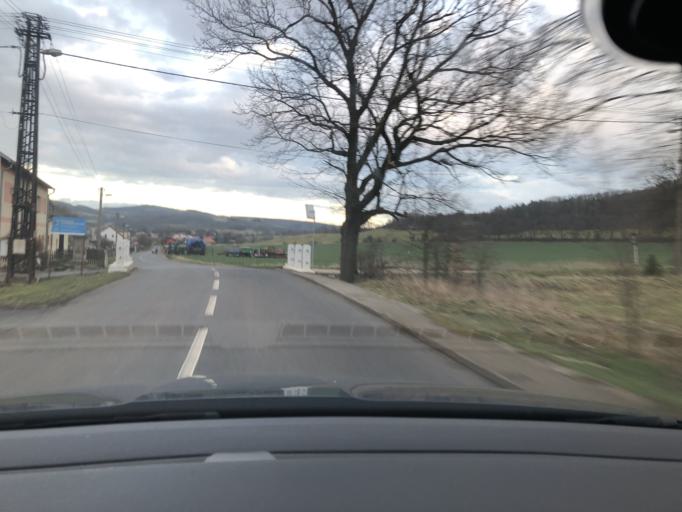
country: CZ
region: Ustecky
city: Rehlovice
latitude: 50.6062
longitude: 13.9365
